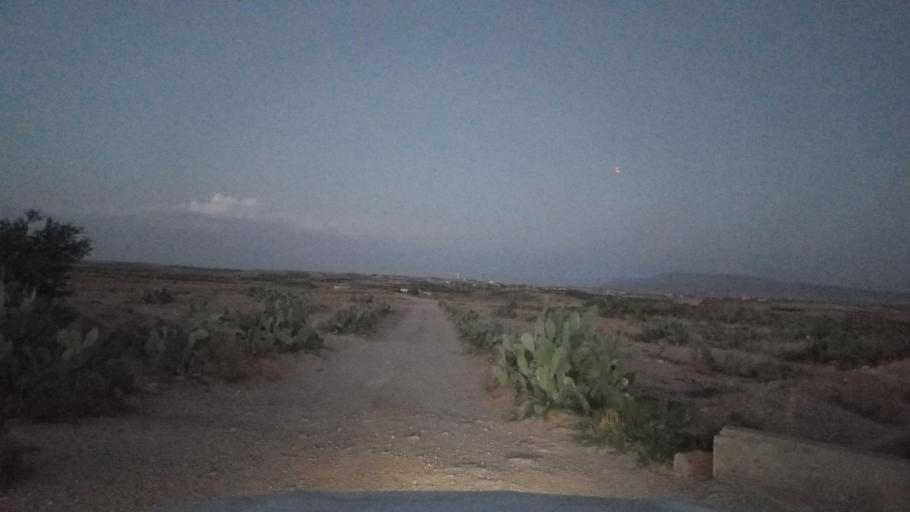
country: TN
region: Al Qasrayn
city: Sbiba
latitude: 35.3788
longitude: 9.0252
